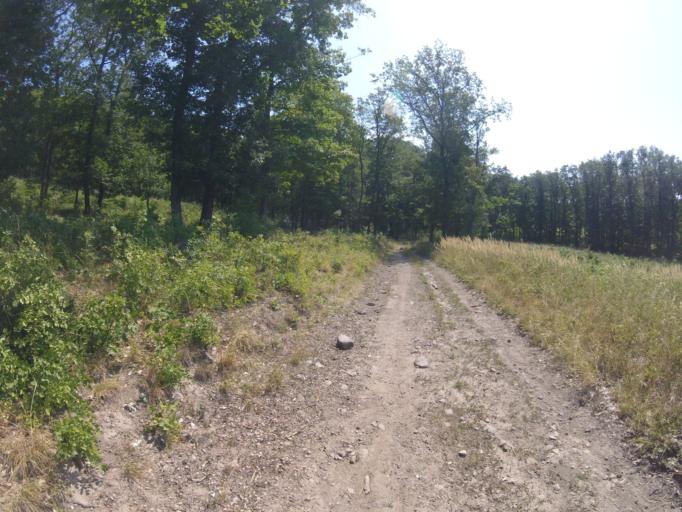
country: HU
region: Pest
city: Csobanka
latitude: 47.6793
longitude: 18.9614
